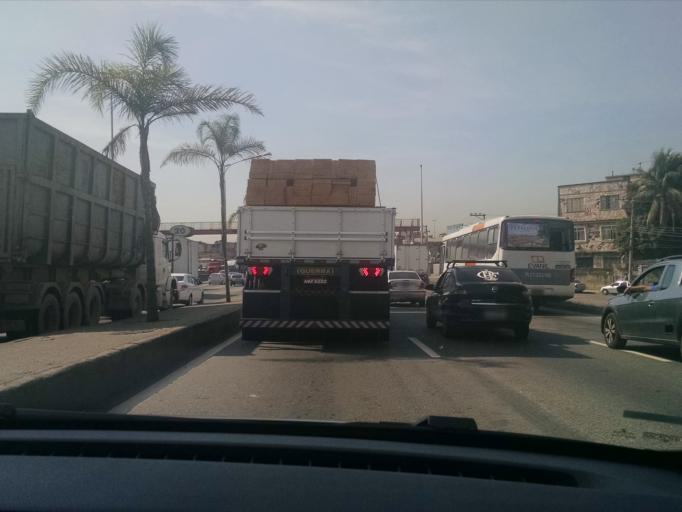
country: BR
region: Rio de Janeiro
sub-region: Duque De Caxias
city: Duque de Caxias
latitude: -22.8148
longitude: -43.2971
